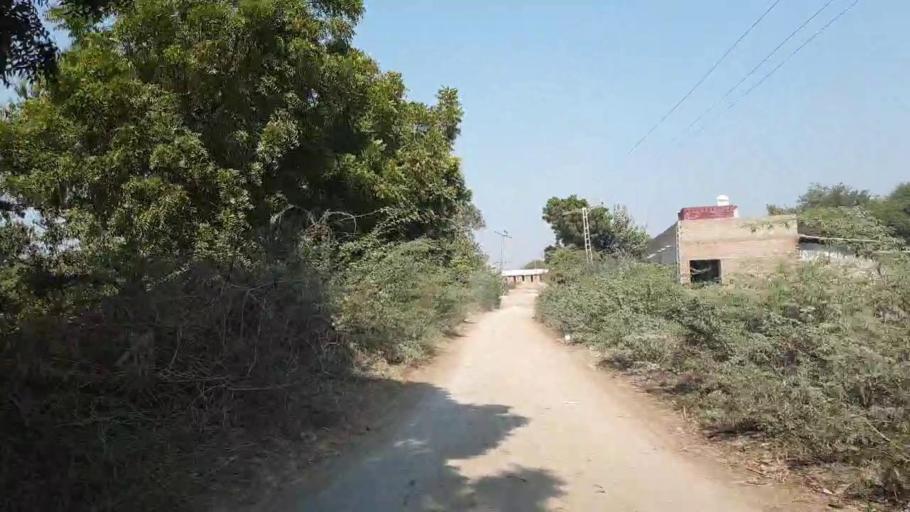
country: PK
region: Sindh
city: Chambar
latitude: 25.4115
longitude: 68.8958
